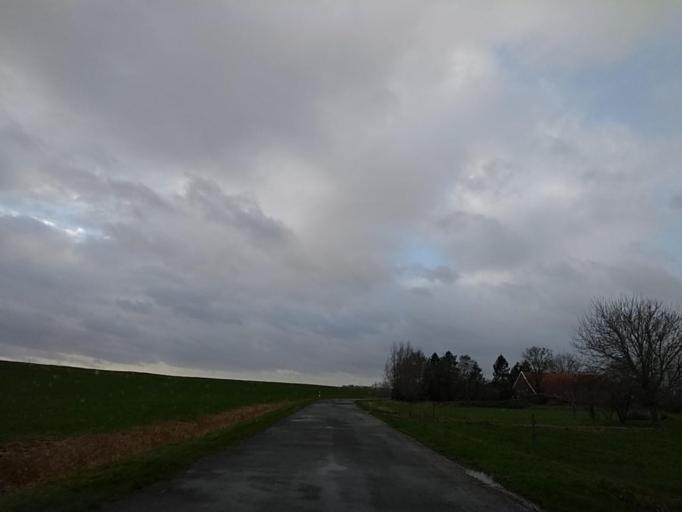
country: DE
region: Lower Saxony
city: Bunde
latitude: 53.2327
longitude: 7.2278
